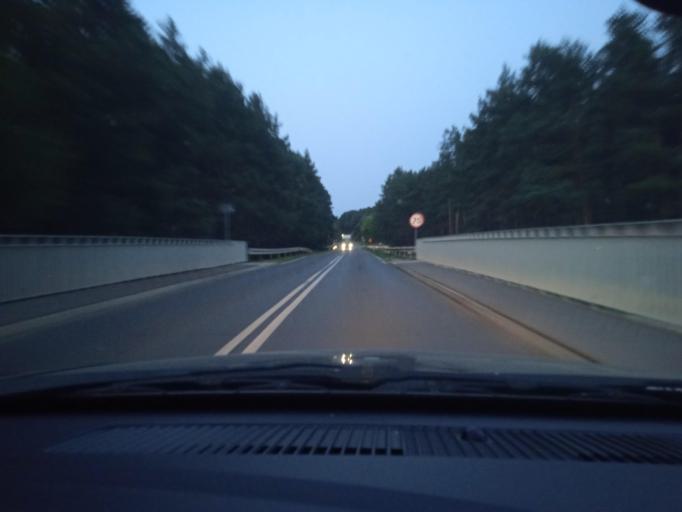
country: PL
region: Masovian Voivodeship
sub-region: Powiat plonski
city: Joniec
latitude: 52.5619
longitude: 20.6659
